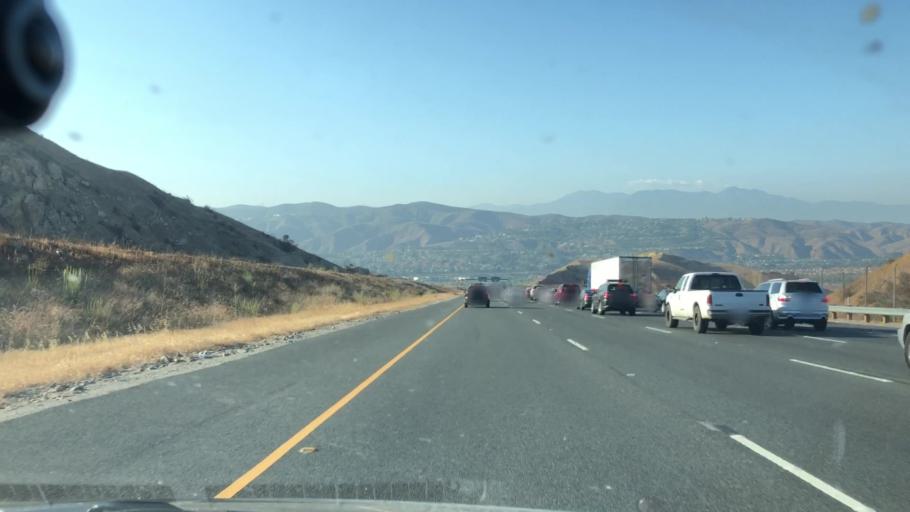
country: US
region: California
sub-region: Orange County
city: Villa Park
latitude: 33.8507
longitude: -117.7168
